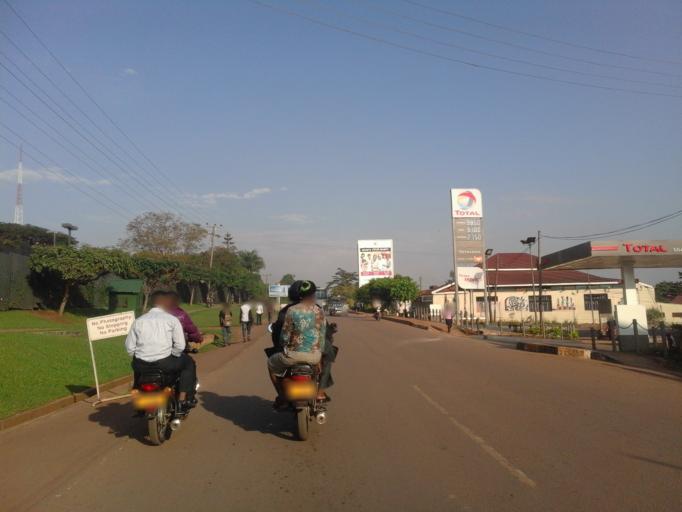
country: UG
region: Central Region
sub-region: Kampala District
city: Kampala
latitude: 0.3007
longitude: 32.5931
